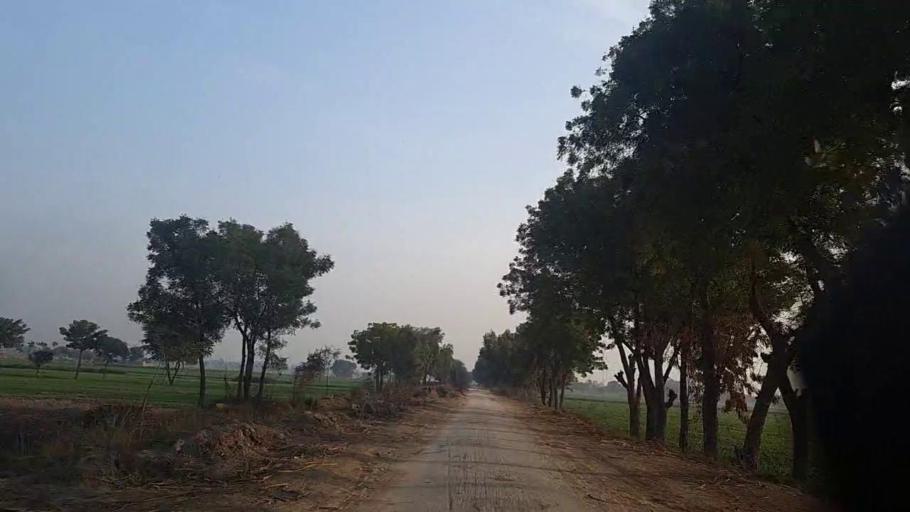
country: PK
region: Sindh
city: Sakrand
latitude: 26.1229
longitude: 68.2308
